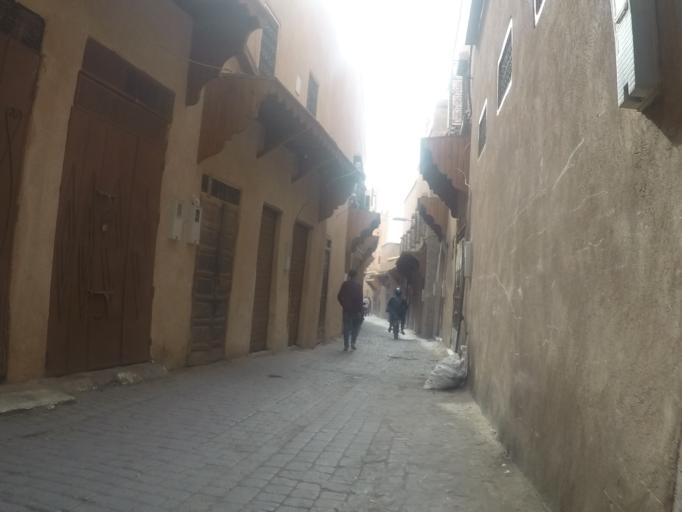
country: MA
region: Marrakech-Tensift-Al Haouz
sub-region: Marrakech
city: Marrakesh
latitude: 31.6299
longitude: -7.9837
